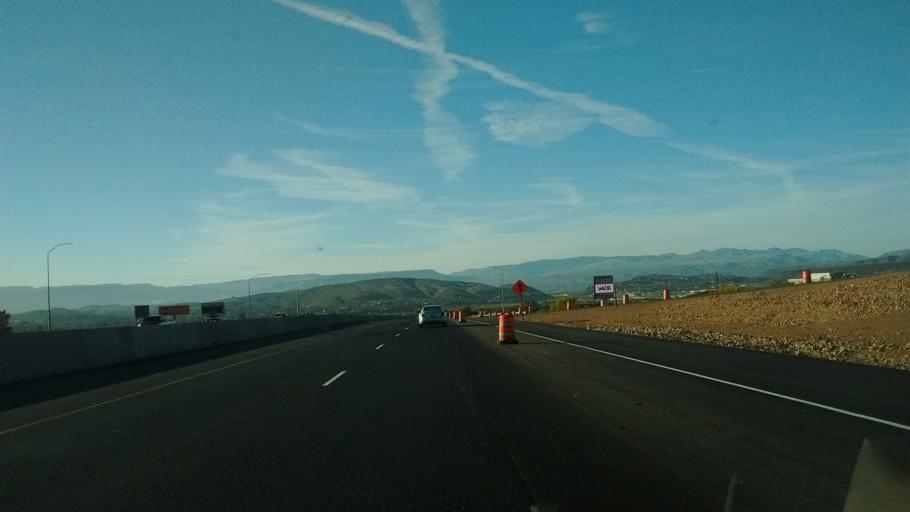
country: US
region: Utah
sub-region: Washington County
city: Saint George
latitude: 37.1085
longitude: -113.5587
